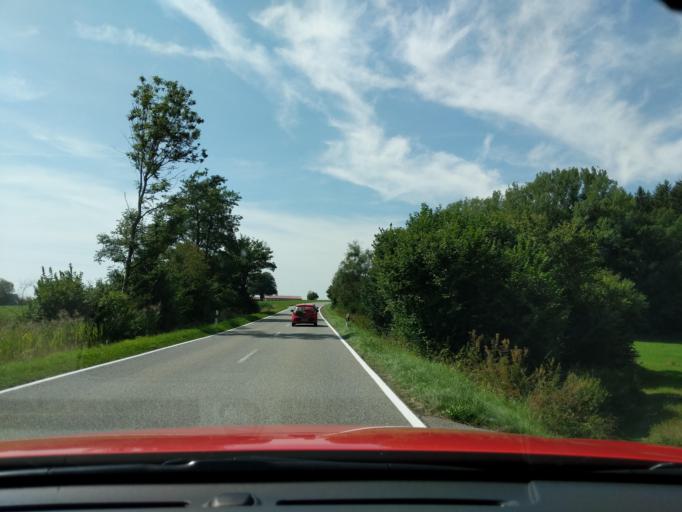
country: DE
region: Baden-Wuerttemberg
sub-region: Tuebingen Region
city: Vogt
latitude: 47.7720
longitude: 9.7830
